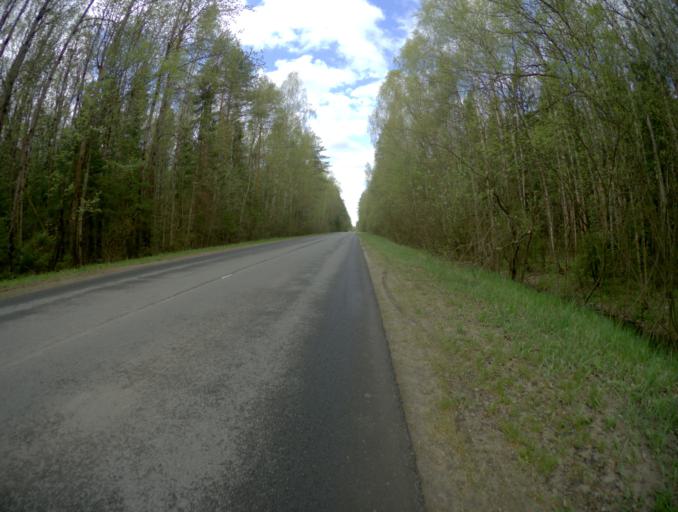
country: RU
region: Vladimir
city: Golovino
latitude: 55.9639
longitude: 40.5274
